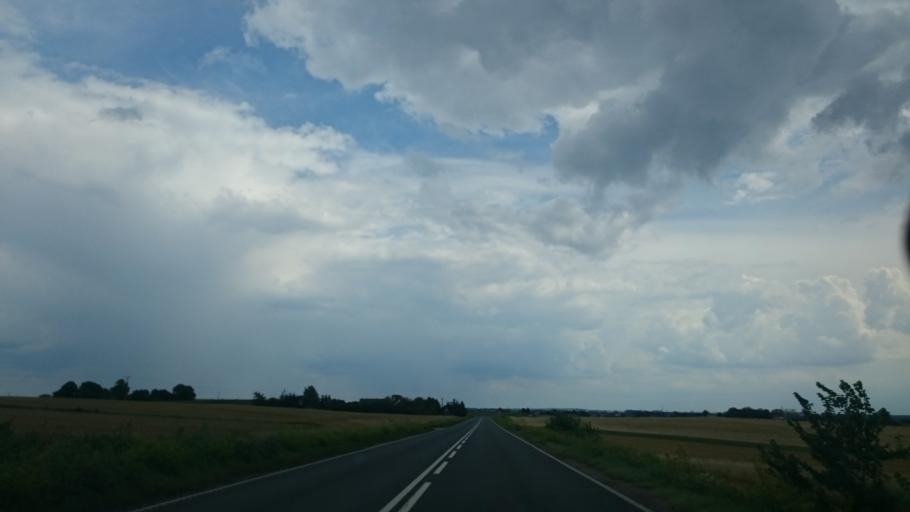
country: PL
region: Kujawsko-Pomorskie
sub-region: Powiat tucholski
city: Kesowo
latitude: 53.6619
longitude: 17.6765
